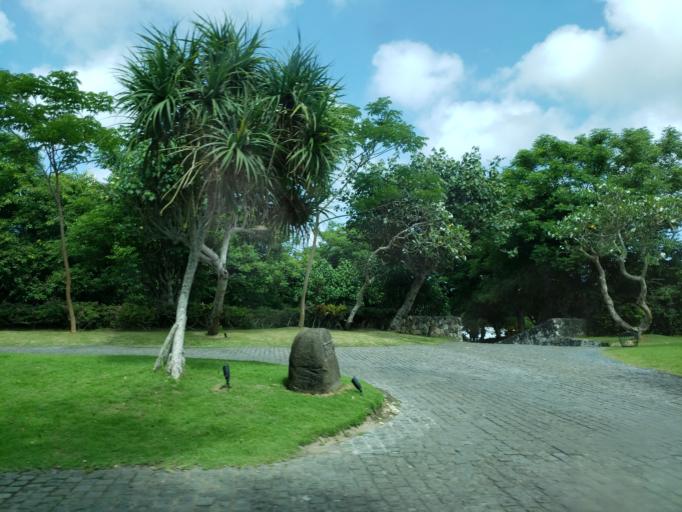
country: ID
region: Bali
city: Pecatu
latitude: -8.8435
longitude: 115.1211
